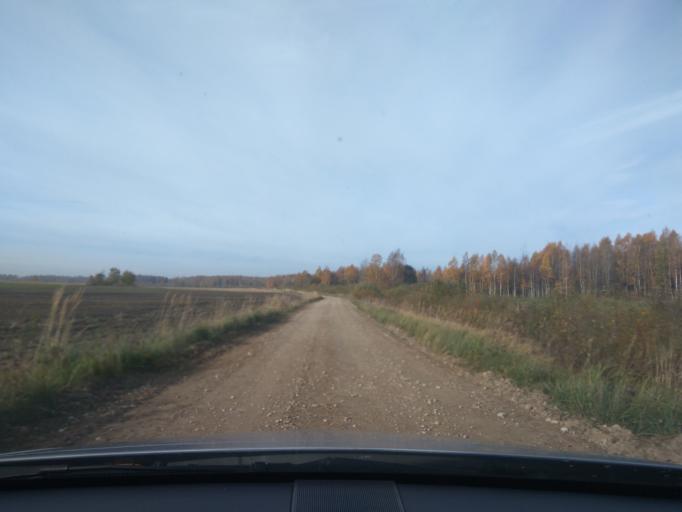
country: LV
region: Aizpute
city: Aizpute
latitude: 56.8452
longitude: 21.7042
